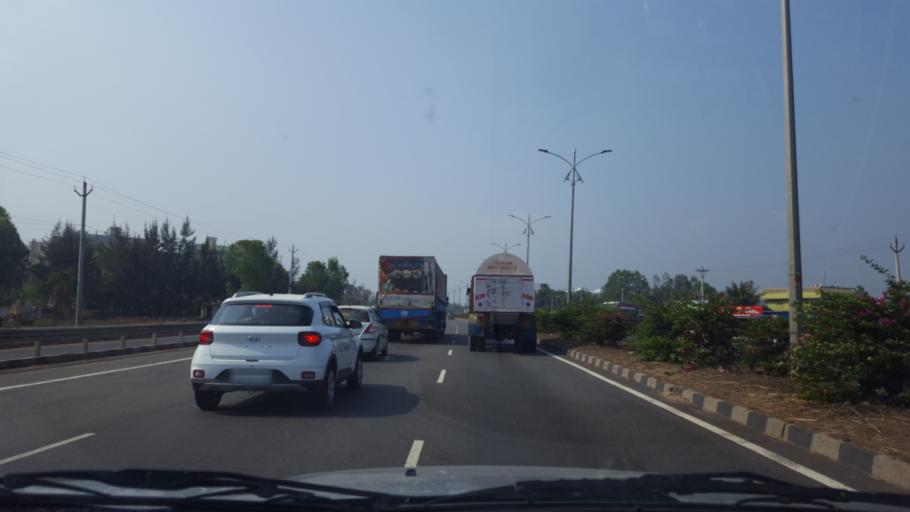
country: IN
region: Andhra Pradesh
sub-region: Vishakhapatnam
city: Bhimunipatnam
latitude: 17.9210
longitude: 83.4179
